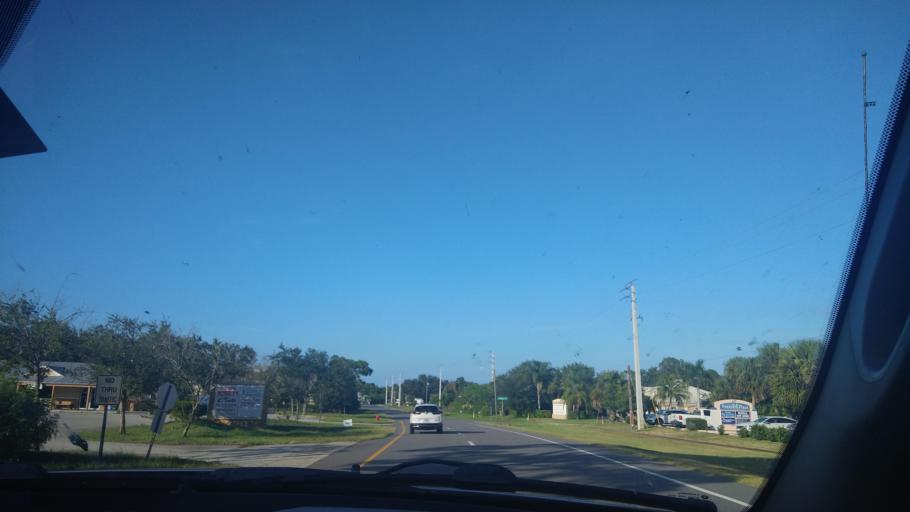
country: US
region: Florida
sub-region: Indian River County
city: Sebastian
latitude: 27.8051
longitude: -80.4732
